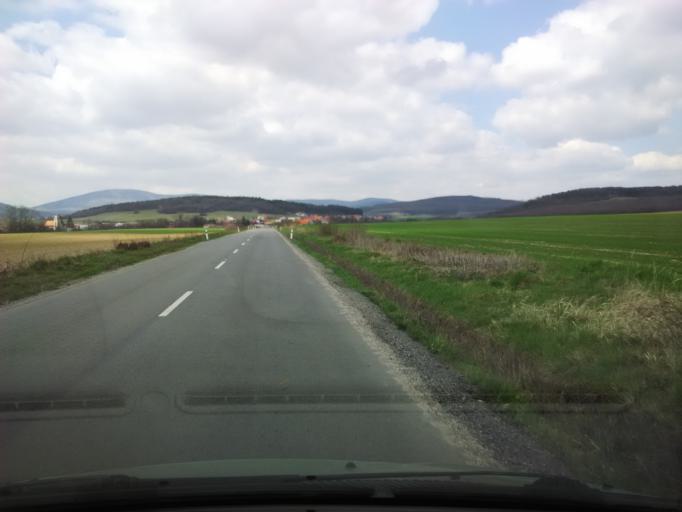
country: SK
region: Nitriansky
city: Zlate Moravce
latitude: 48.4223
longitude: 18.3337
